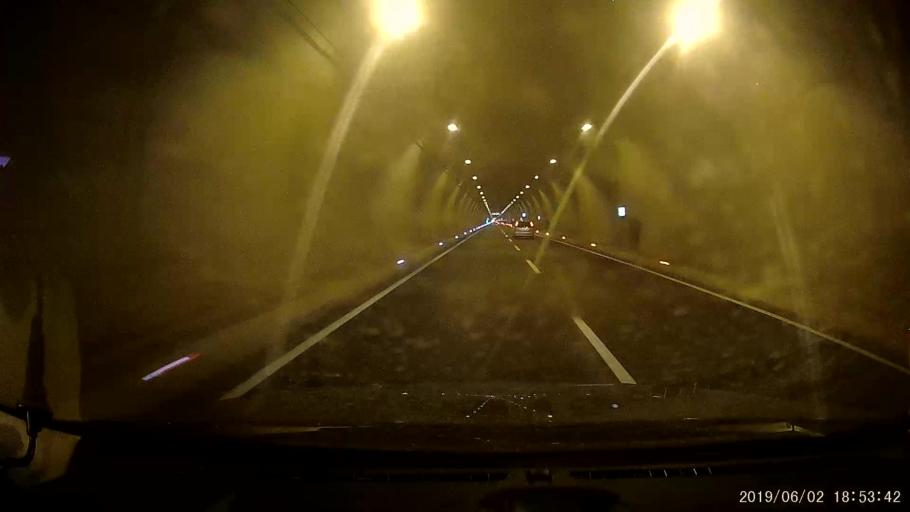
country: TR
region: Ordu
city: Ordu
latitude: 40.9758
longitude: 37.8361
